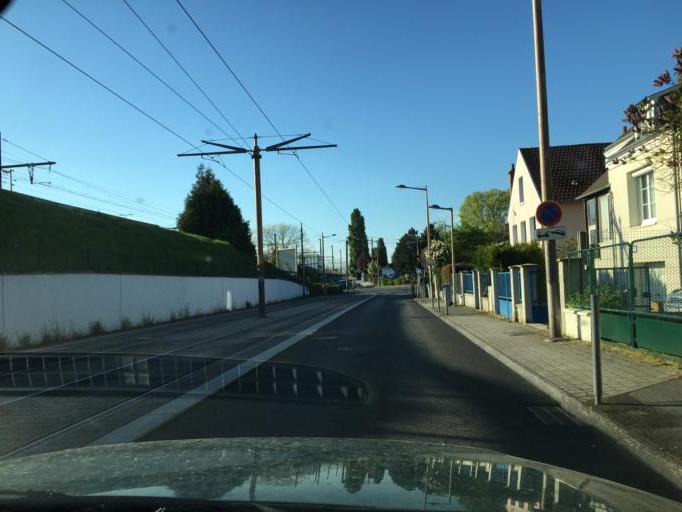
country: FR
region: Centre
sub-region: Departement du Loiret
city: Fleury-les-Aubrais
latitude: 47.9280
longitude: 1.9064
